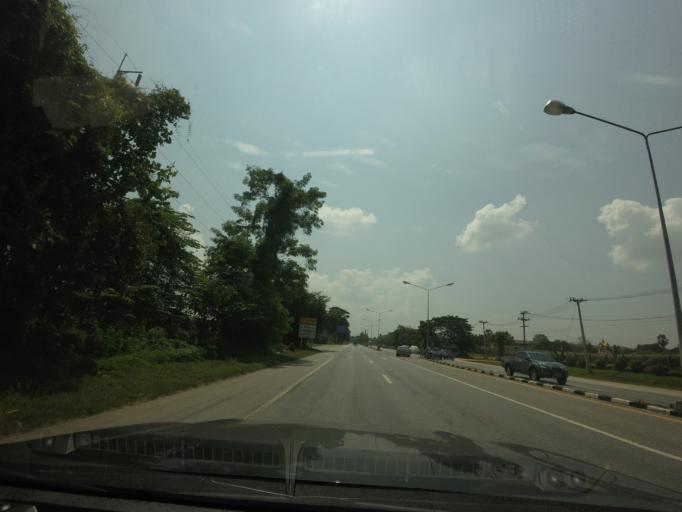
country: TH
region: Uttaradit
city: Uttaradit
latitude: 17.6150
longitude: 100.1238
